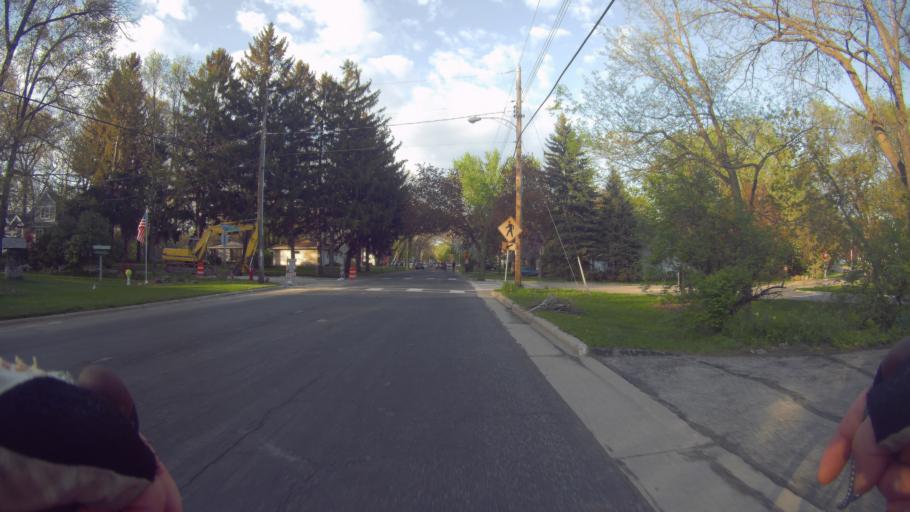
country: US
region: Wisconsin
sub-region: Dane County
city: Monona
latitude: 43.0675
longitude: -89.3412
